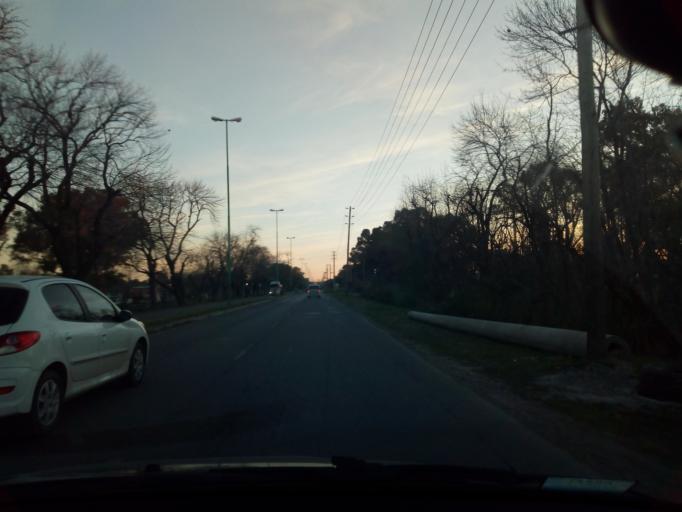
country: AR
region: Buenos Aires
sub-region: Partido de Ensenada
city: Ensenada
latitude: -34.8736
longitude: -57.9152
